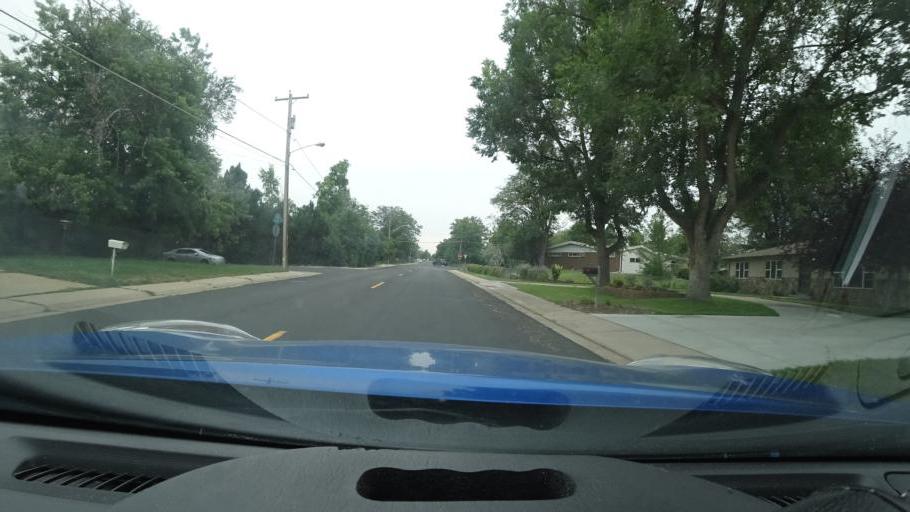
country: US
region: Colorado
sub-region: Arapahoe County
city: Glendale
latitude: 39.6829
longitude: -104.9082
